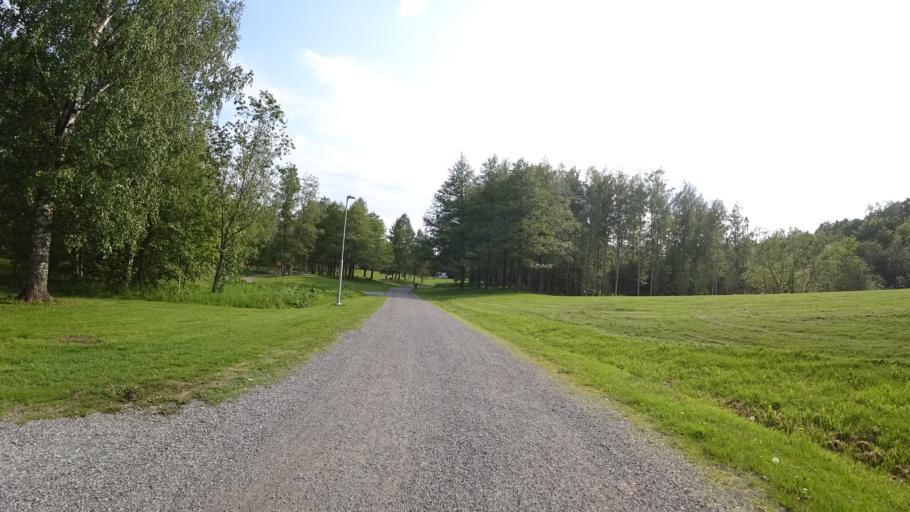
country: FI
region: Pirkanmaa
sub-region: Tampere
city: Pirkkala
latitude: 61.5042
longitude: 23.6634
